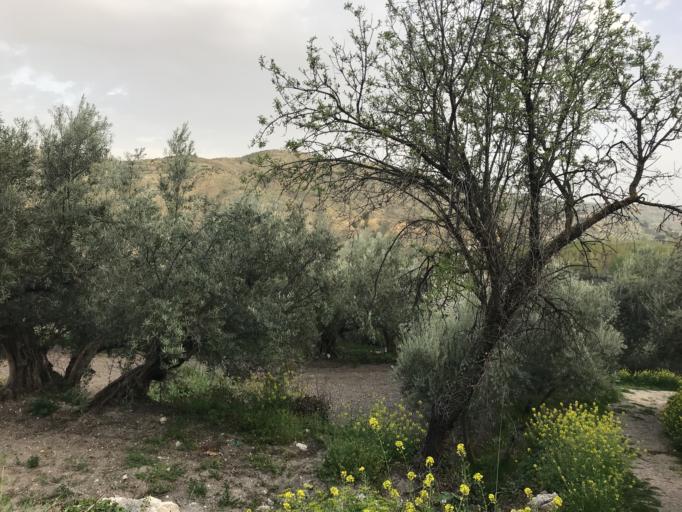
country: ES
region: Andalusia
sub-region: Provincia de Granada
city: Castril
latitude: 37.7928
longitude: -2.7793
